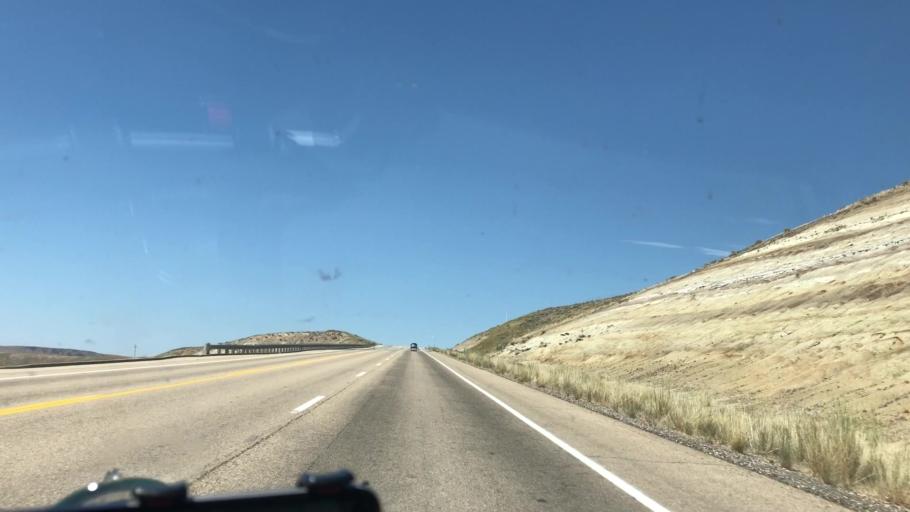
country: US
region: Idaho
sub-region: Owyhee County
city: Marsing
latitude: 43.2909
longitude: -116.9859
